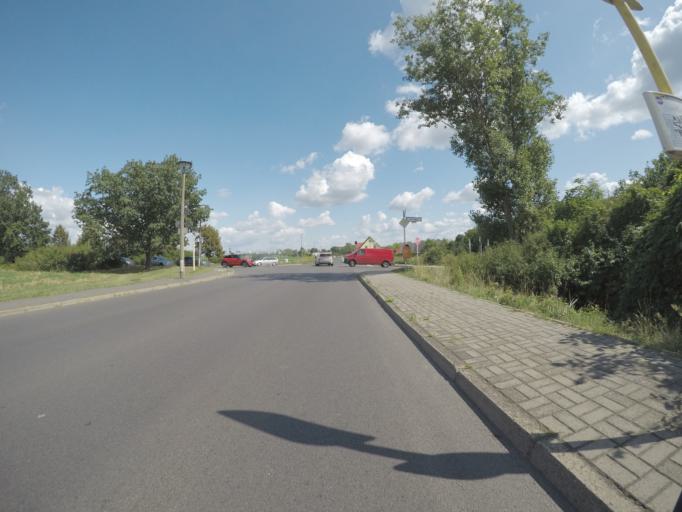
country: DE
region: Berlin
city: Kaulsdorf
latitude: 52.5024
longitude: 13.5970
